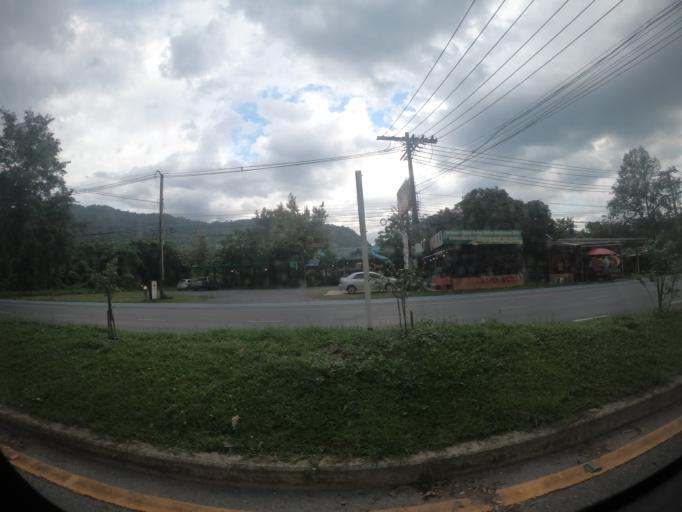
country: TH
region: Nakhon Nayok
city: Nakhon Nayok
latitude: 14.3217
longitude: 101.3119
